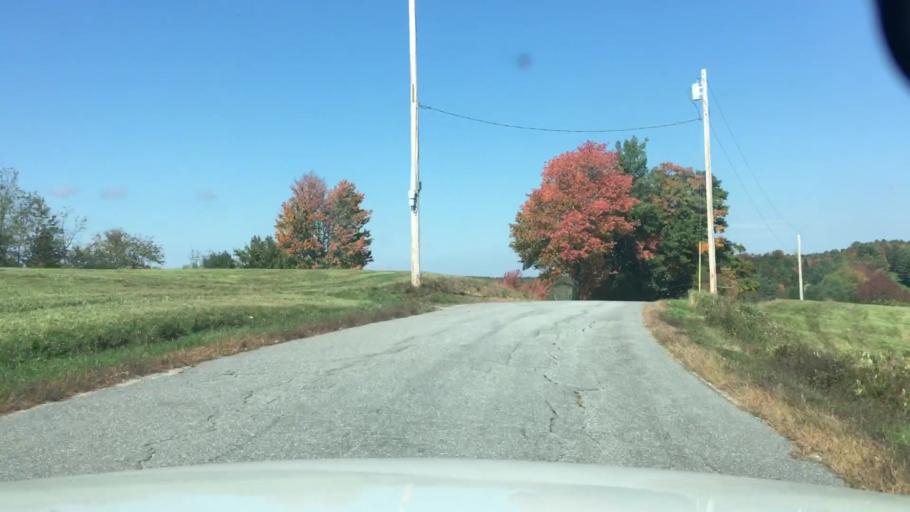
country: US
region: Maine
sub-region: Sagadahoc County
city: Topsham
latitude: 44.0109
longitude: -69.9616
